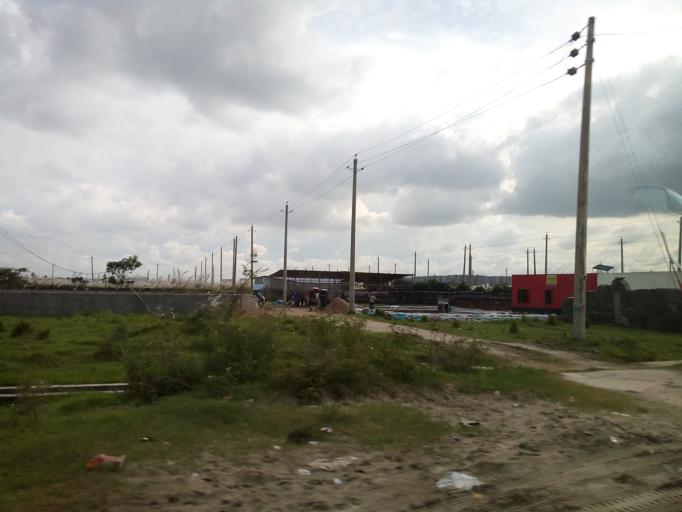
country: BD
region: Dhaka
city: Tungi
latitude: 23.8679
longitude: 90.3662
